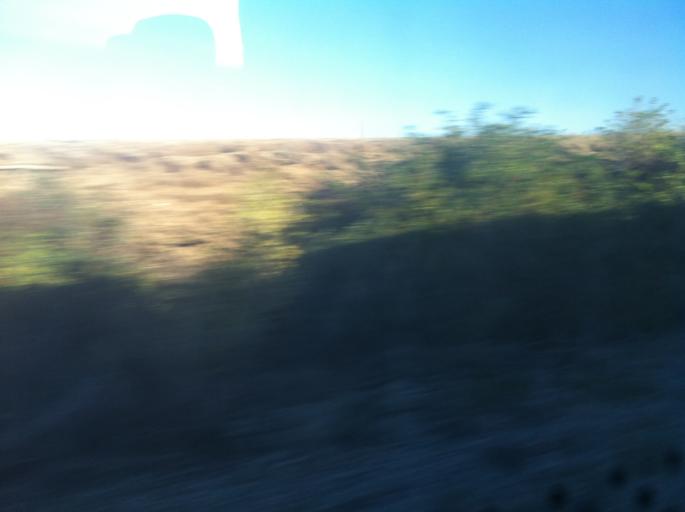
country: ES
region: Castille and Leon
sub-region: Provincia de Palencia
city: Reinoso de Cerrato
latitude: 42.0044
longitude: -4.3526
